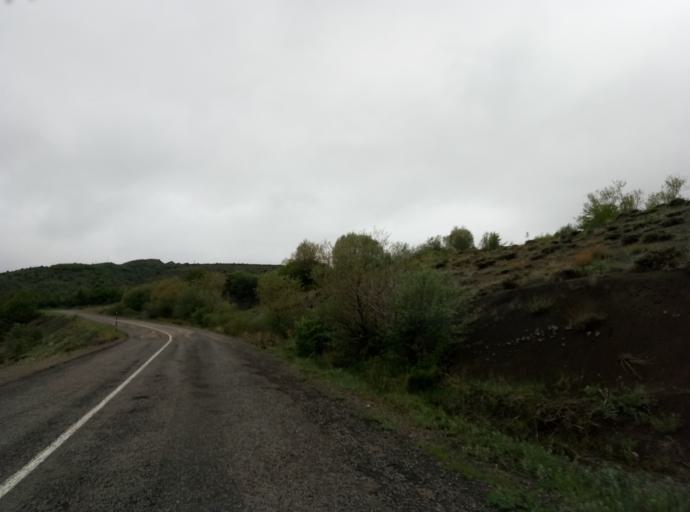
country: TR
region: Sivas
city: Serefiye
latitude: 40.1687
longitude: 37.8916
